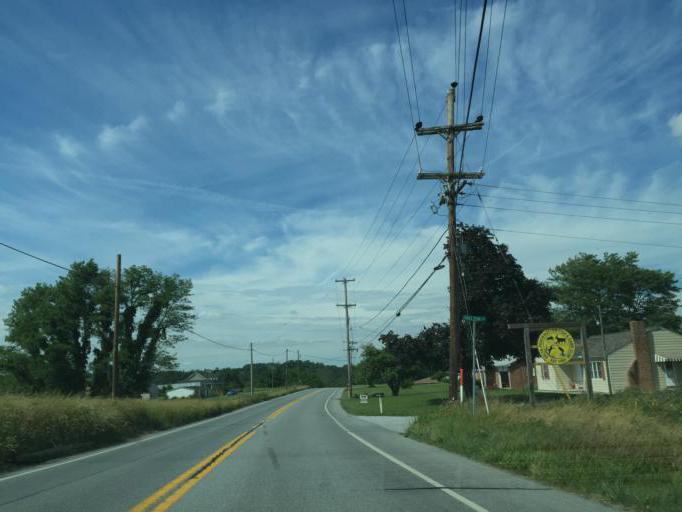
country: US
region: Pennsylvania
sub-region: York County
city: Susquehanna Trails
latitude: 39.7583
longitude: -76.3291
